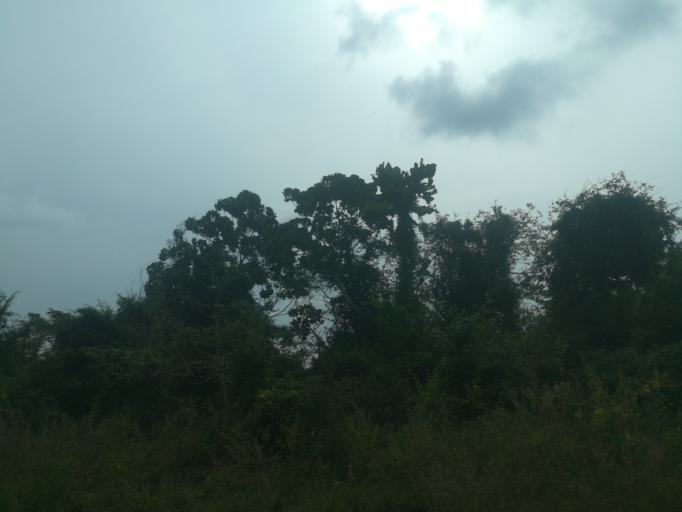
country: NG
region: Ogun
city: Ayetoro
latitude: 7.2736
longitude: 3.1000
